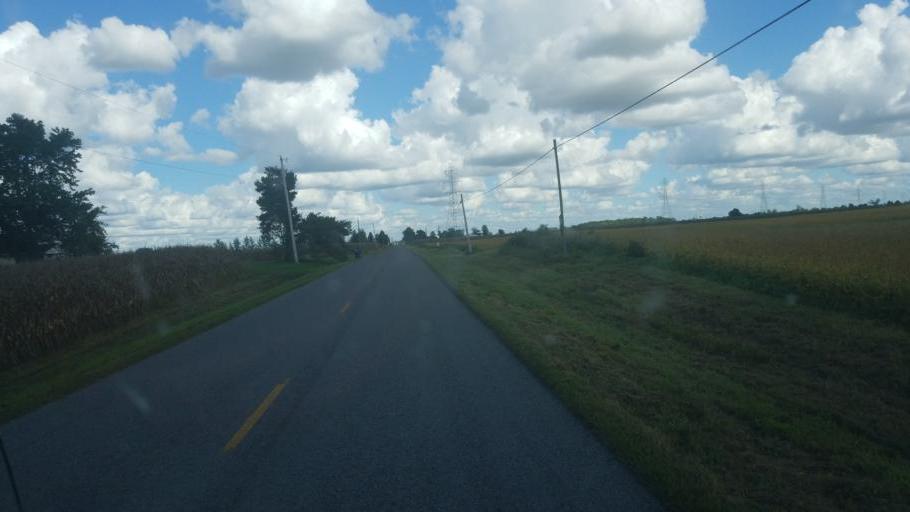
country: US
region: Ohio
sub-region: Logan County
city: Northwood
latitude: 40.5035
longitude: -83.6041
